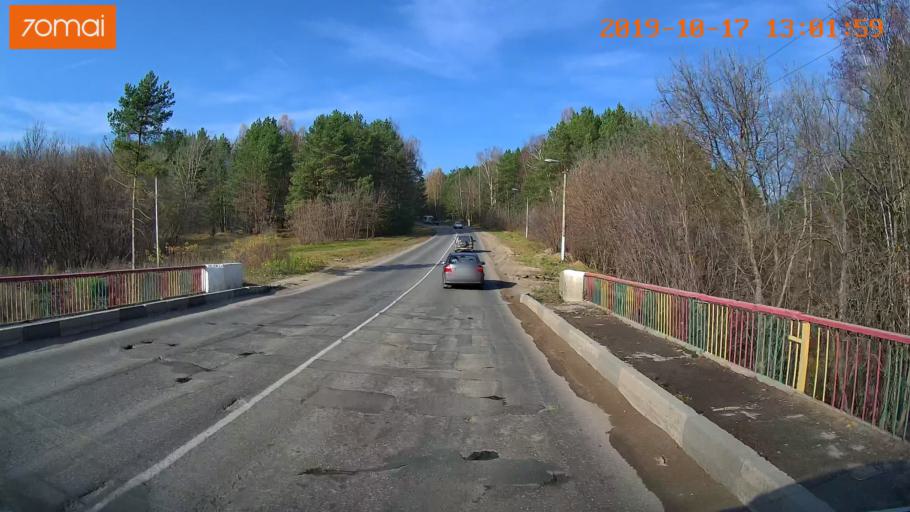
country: RU
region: Rjazan
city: Kasimov
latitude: 54.9474
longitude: 41.3644
